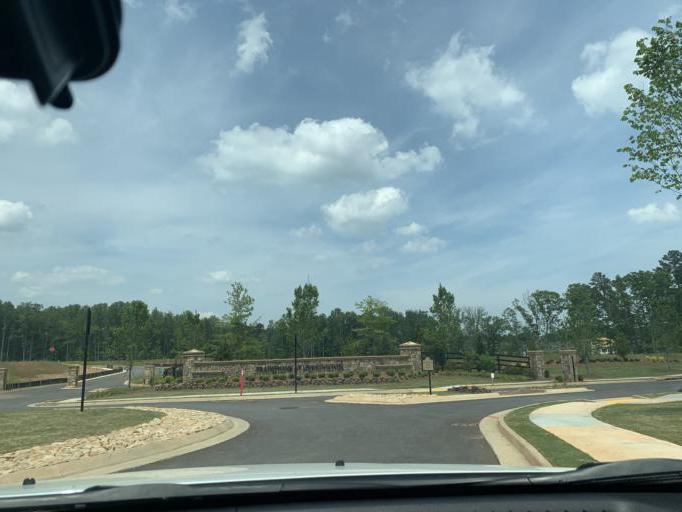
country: US
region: Georgia
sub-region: Forsyth County
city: Cumming
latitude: 34.1557
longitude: -84.1671
